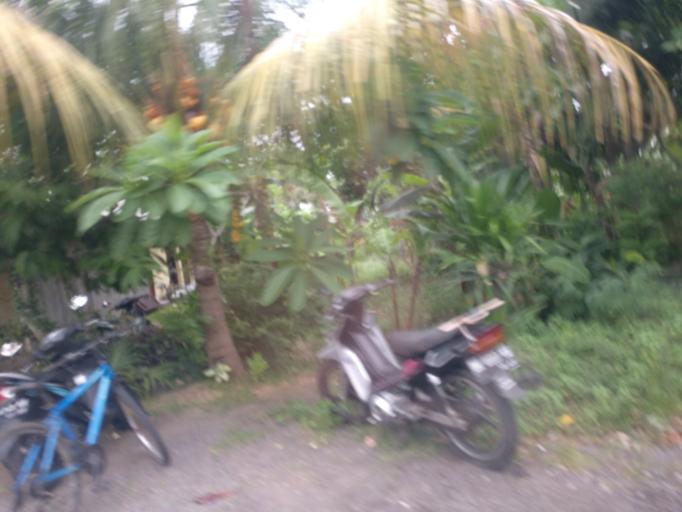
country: ID
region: Bali
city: Banjar Pasekan
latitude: -8.6074
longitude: 115.3154
